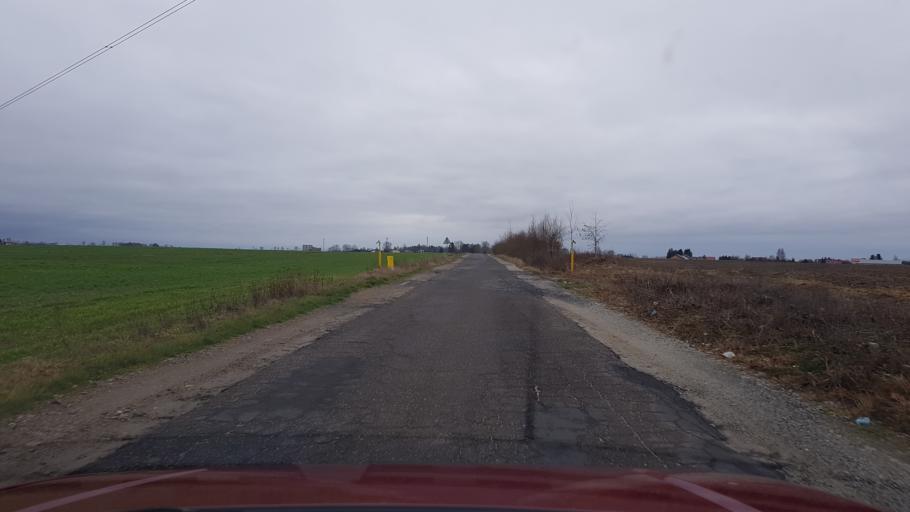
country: PL
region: West Pomeranian Voivodeship
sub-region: Powiat koszalinski
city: Mielno
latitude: 54.1465
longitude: 16.0309
